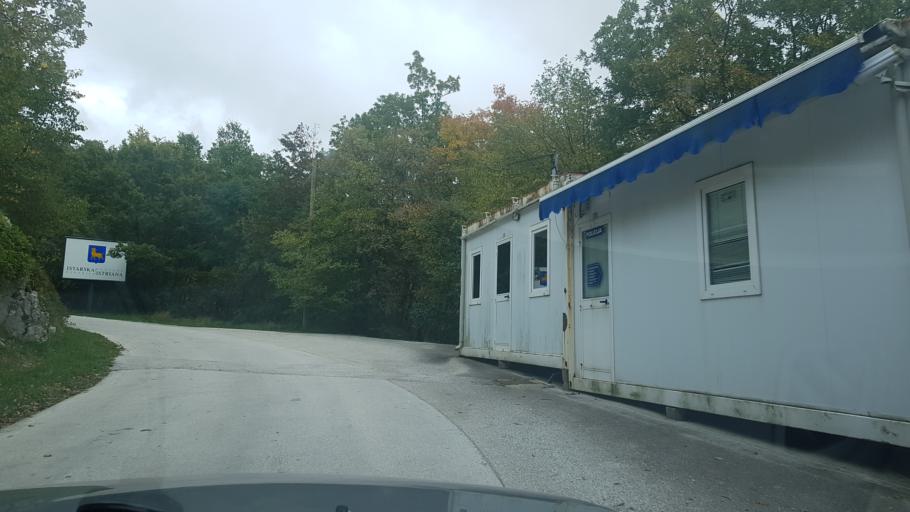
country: HR
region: Istarska
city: Buzet
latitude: 45.5094
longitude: 13.9678
